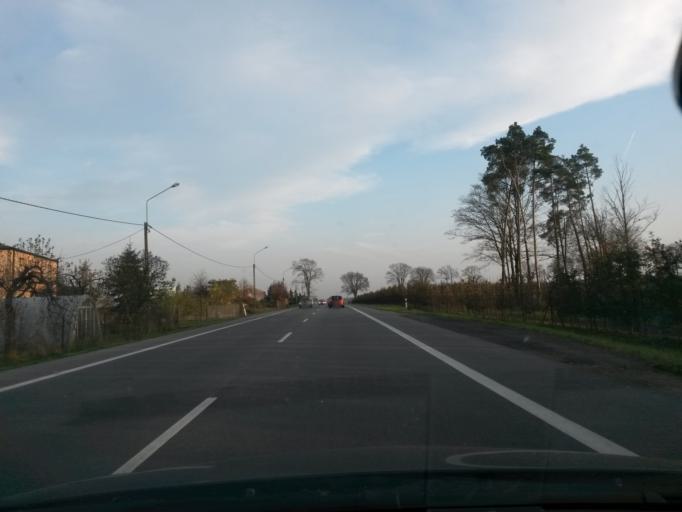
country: PL
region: Lodz Voivodeship
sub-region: Powiat wielunski
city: Czarnozyly
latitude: 51.2528
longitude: 18.5052
